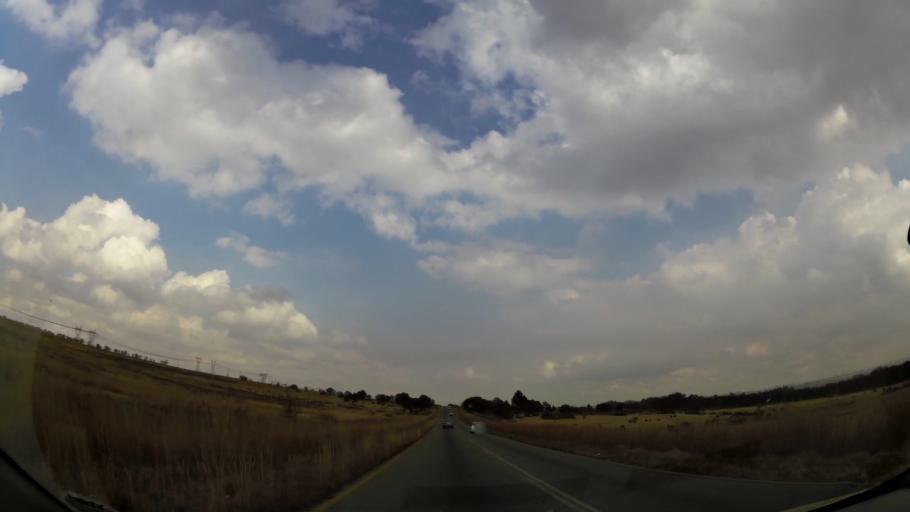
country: ZA
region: Orange Free State
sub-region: Fezile Dabi District Municipality
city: Sasolburg
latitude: -26.7840
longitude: 27.9180
